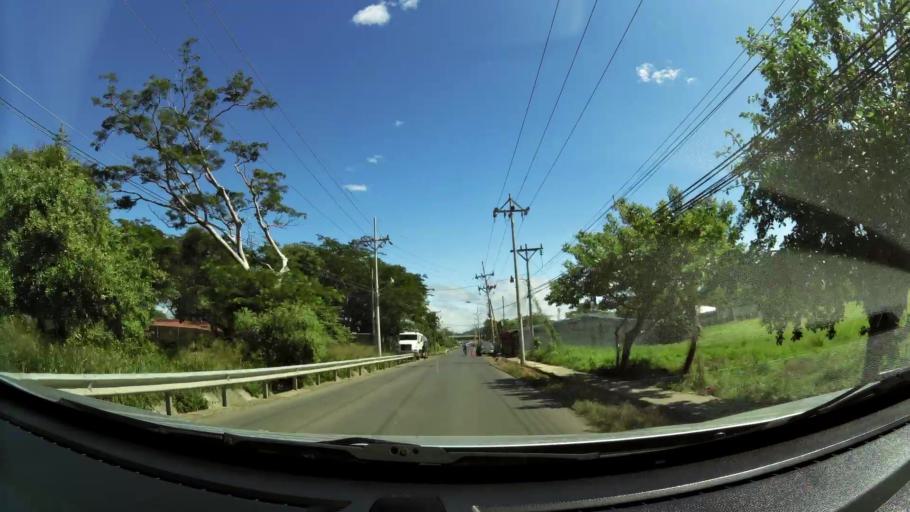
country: CR
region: Guanacaste
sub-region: Canton de Canas
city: Canas
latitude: 10.4252
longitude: -85.0967
